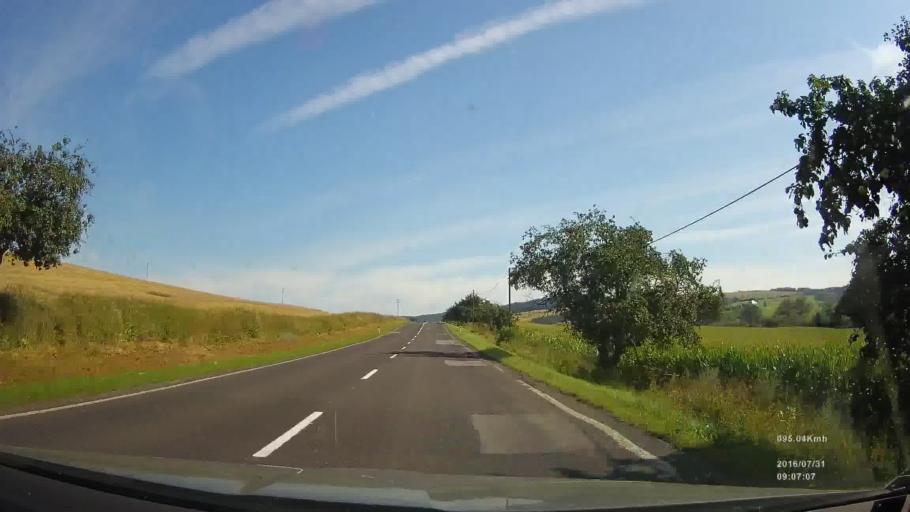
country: SK
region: Presovsky
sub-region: Okres Bardejov
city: Bardejov
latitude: 49.1796
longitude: 21.3067
